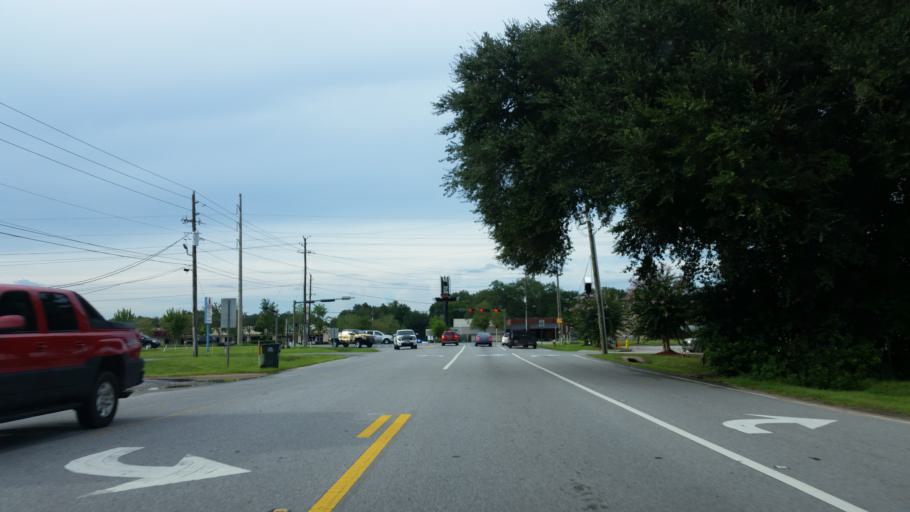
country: US
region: Florida
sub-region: Santa Rosa County
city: Pace
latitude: 30.6022
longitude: -87.1111
